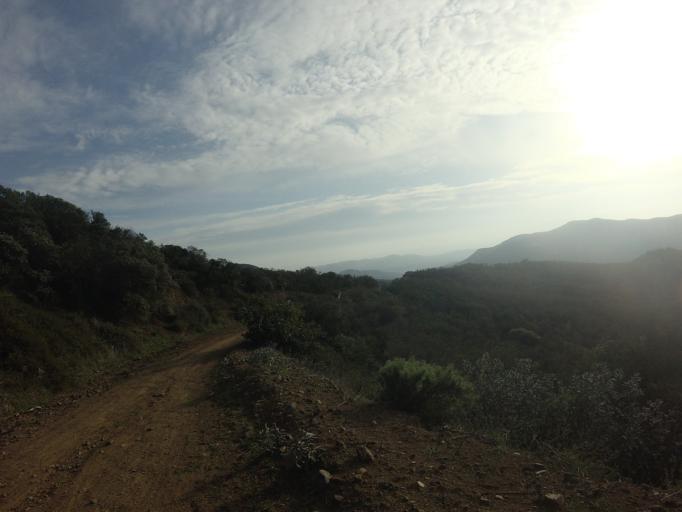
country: US
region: California
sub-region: Riverside County
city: Corona
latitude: 33.8197
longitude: -117.6399
